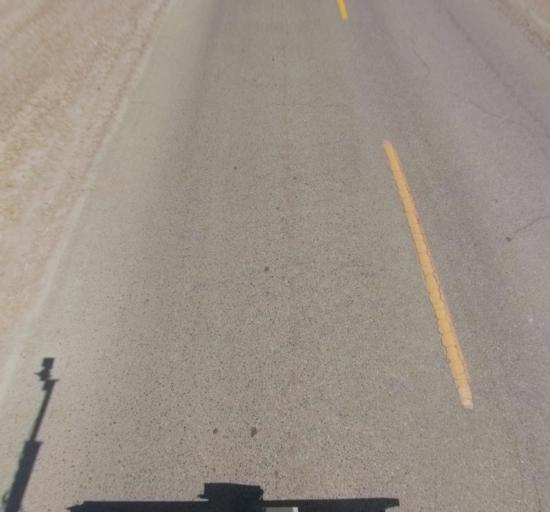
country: US
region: California
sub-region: Fresno County
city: Mendota
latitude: 36.8132
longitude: -120.2592
